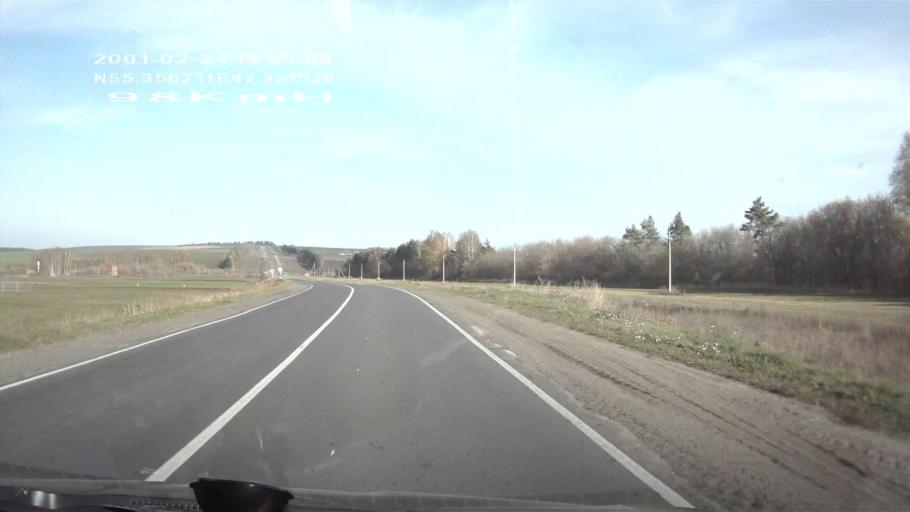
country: RU
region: Chuvashia
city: Ibresi
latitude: 55.3563
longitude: 47.2312
